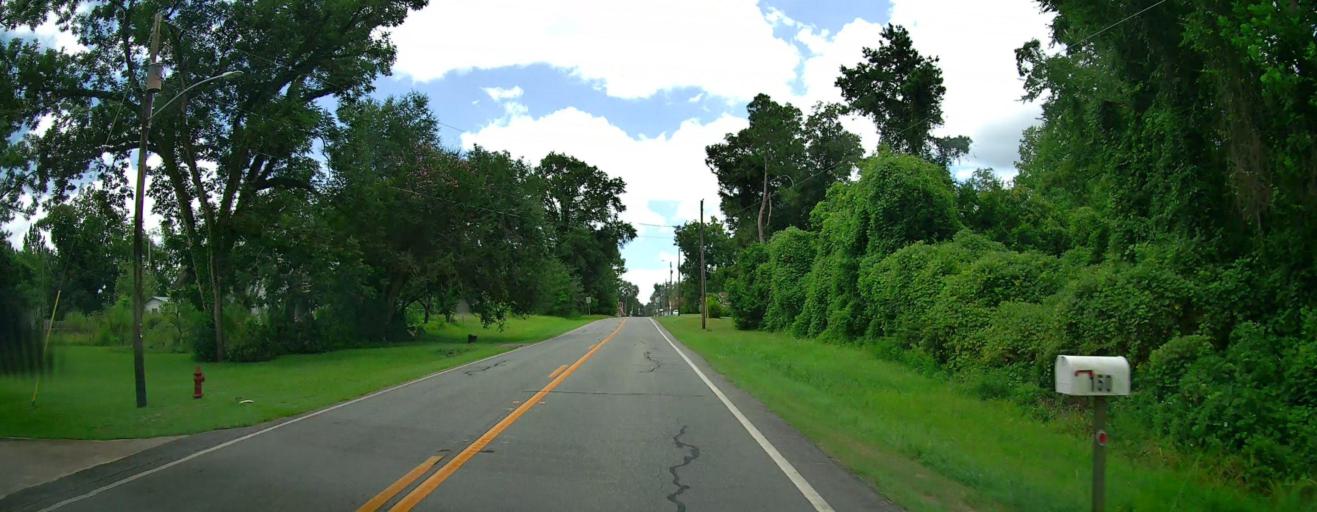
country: US
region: Georgia
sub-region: Wilcox County
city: Rochelle
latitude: 31.9499
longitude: -83.5407
